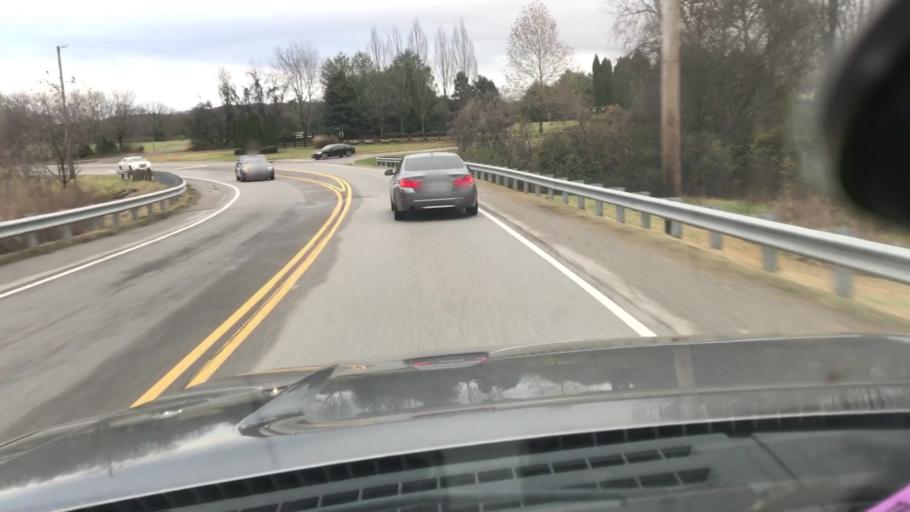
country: US
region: Tennessee
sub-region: Williamson County
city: Brentwood Estates
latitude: 35.9660
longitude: -86.7791
